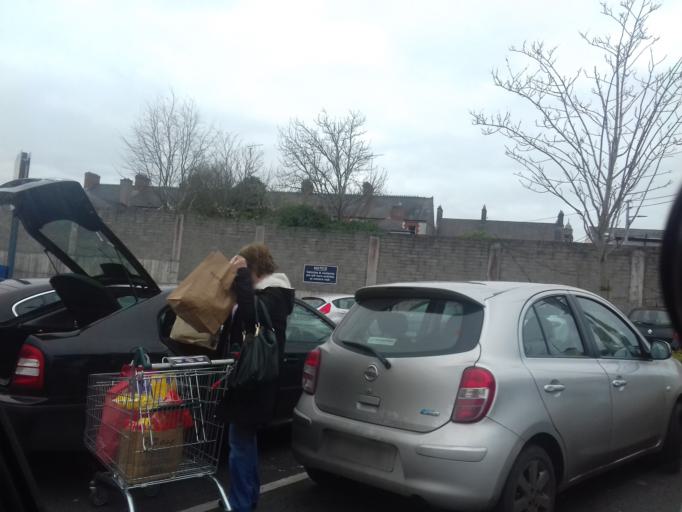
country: IE
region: Leinster
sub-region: An Iarmhi
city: An Muileann gCearr
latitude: 53.5287
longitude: -7.3410
